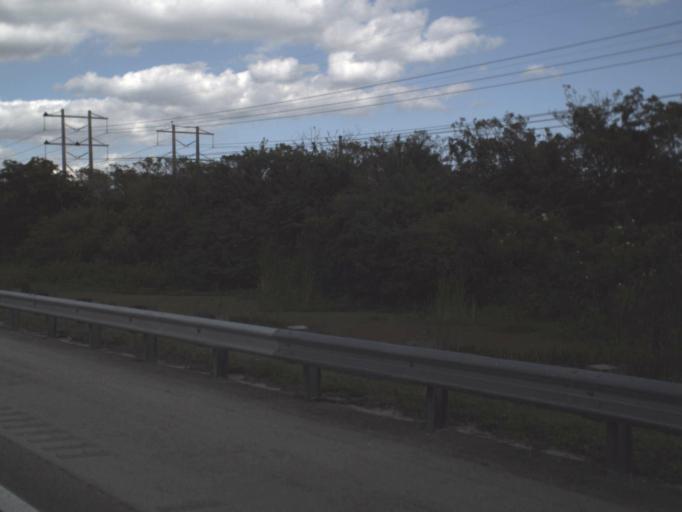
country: US
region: Florida
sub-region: Broward County
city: Davie
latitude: 26.0589
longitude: -80.2151
